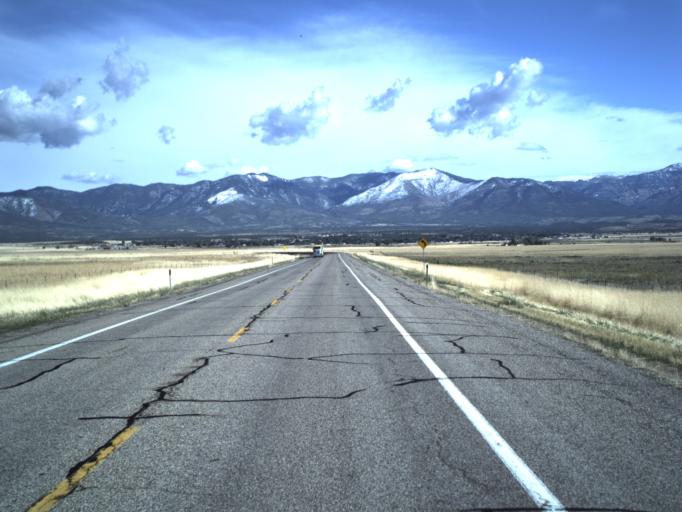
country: US
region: Utah
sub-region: Millard County
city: Fillmore
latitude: 39.1170
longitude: -112.3133
